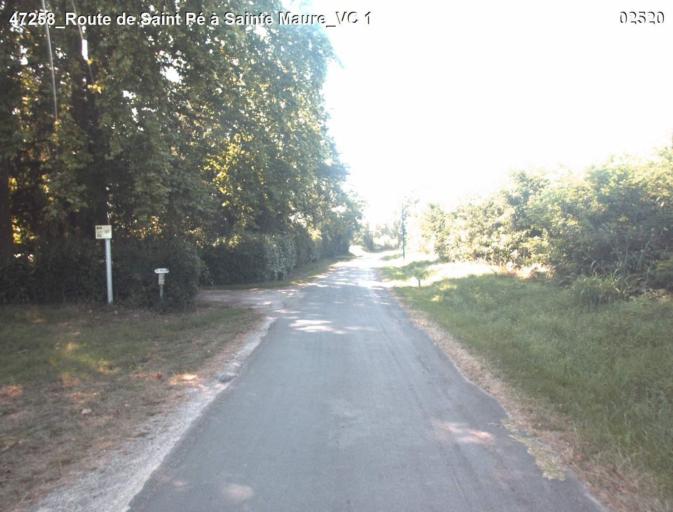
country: FR
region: Midi-Pyrenees
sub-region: Departement du Gers
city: Montreal
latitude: 44.0126
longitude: 0.1502
